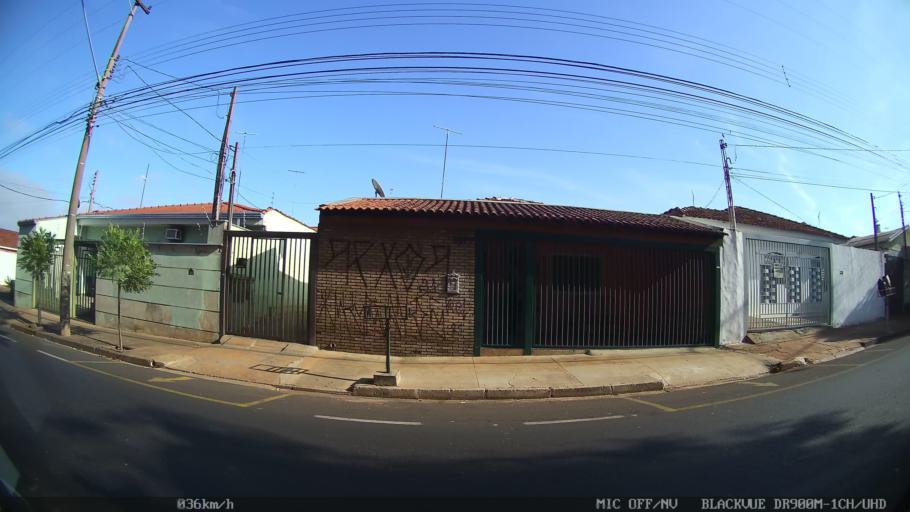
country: BR
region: Sao Paulo
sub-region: Sao Jose Do Rio Preto
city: Sao Jose do Rio Preto
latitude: -20.7854
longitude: -49.4094
